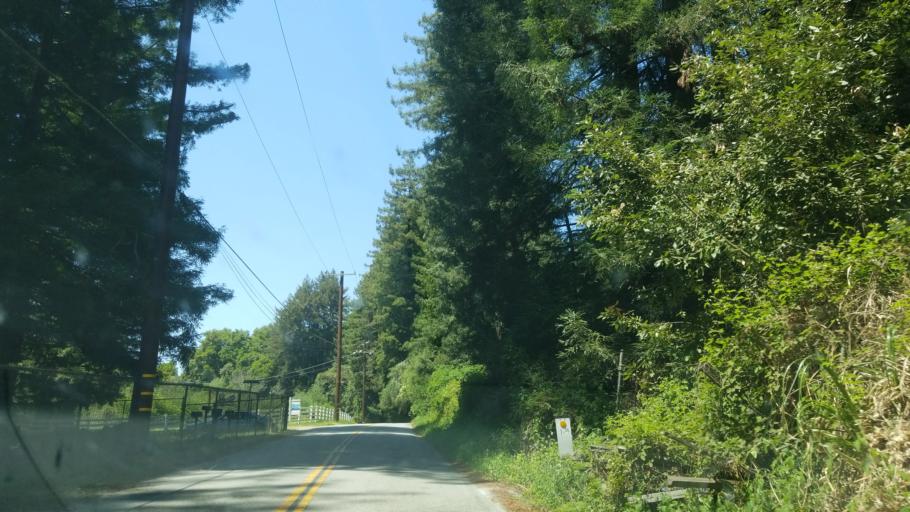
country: US
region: California
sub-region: Santa Cruz County
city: Amesti
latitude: 37.0147
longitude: -121.7536
